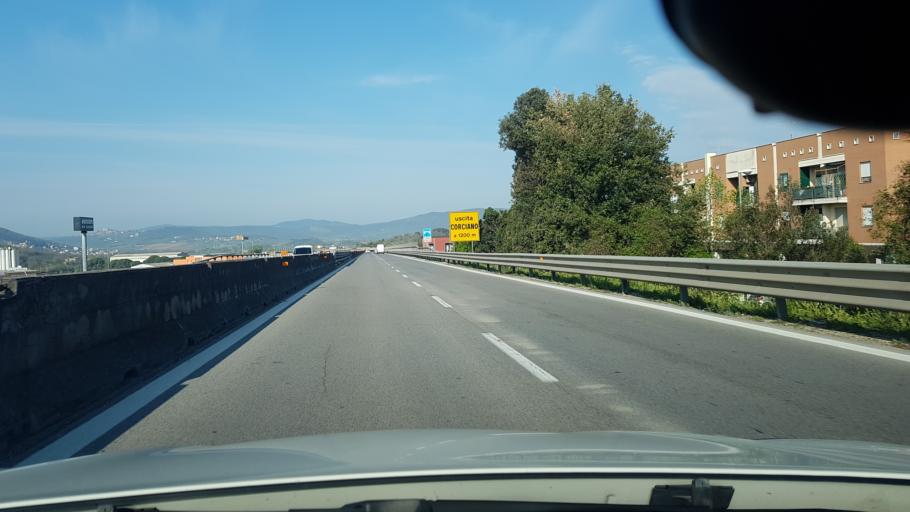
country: IT
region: Umbria
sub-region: Provincia di Perugia
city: Chiugiana-La Commenda
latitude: 43.1018
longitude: 12.3134
